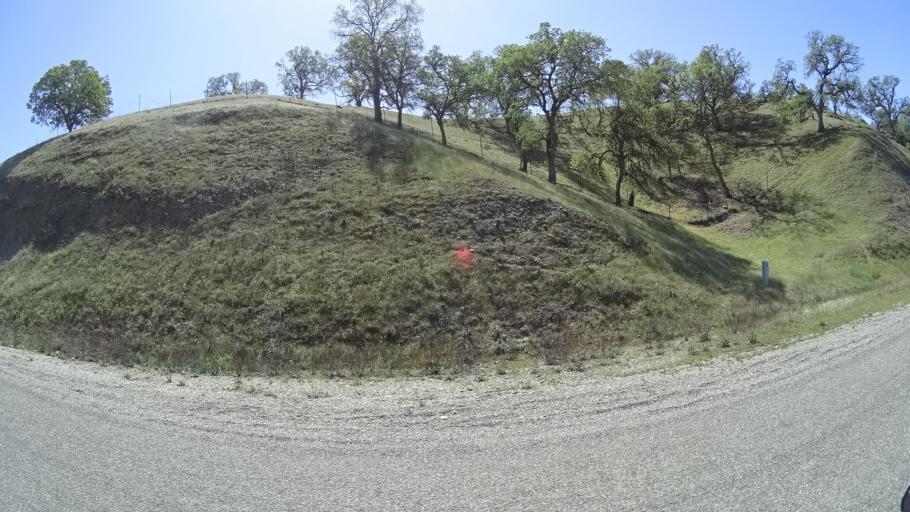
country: US
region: California
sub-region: Glenn County
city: Orland
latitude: 39.7422
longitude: -122.3828
